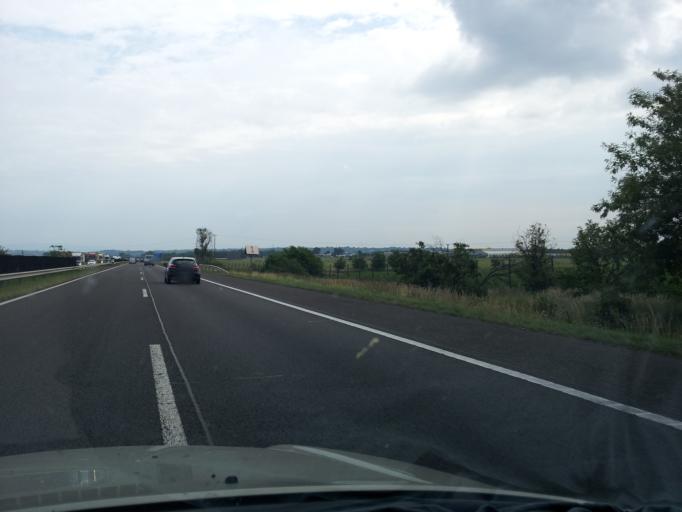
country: HU
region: Heves
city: Hered
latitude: 47.6738
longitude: 19.6402
